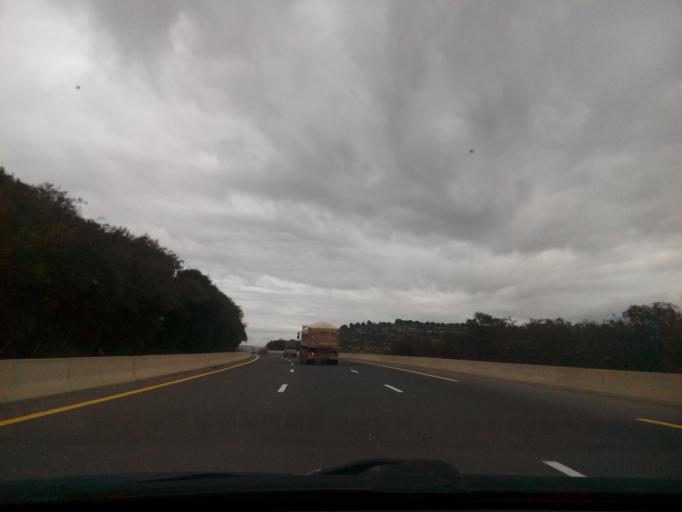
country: DZ
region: Sidi Bel Abbes
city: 'Ain el Berd
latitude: 35.3884
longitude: -0.4896
